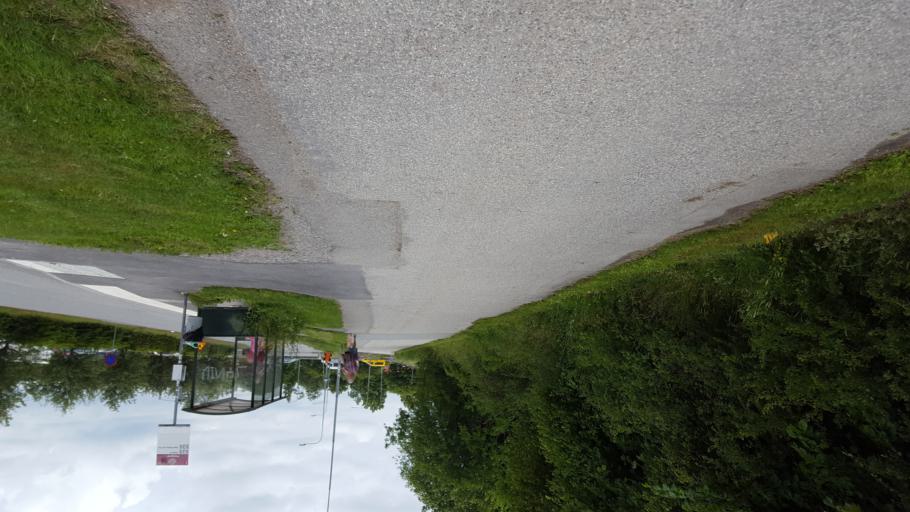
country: SE
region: Stockholm
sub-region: Upplands Vasby Kommun
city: Upplands Vaesby
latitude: 59.5143
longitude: 17.8868
